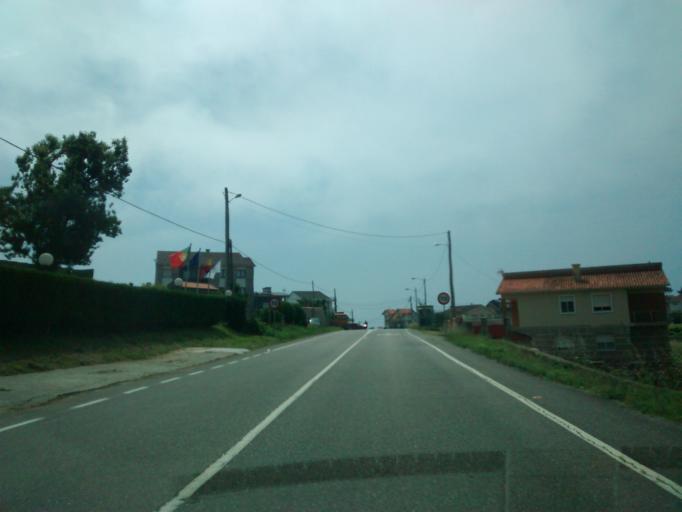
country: ES
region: Galicia
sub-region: Provincia de Pontevedra
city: Sanxenxo
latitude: 42.4062
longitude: -8.8535
